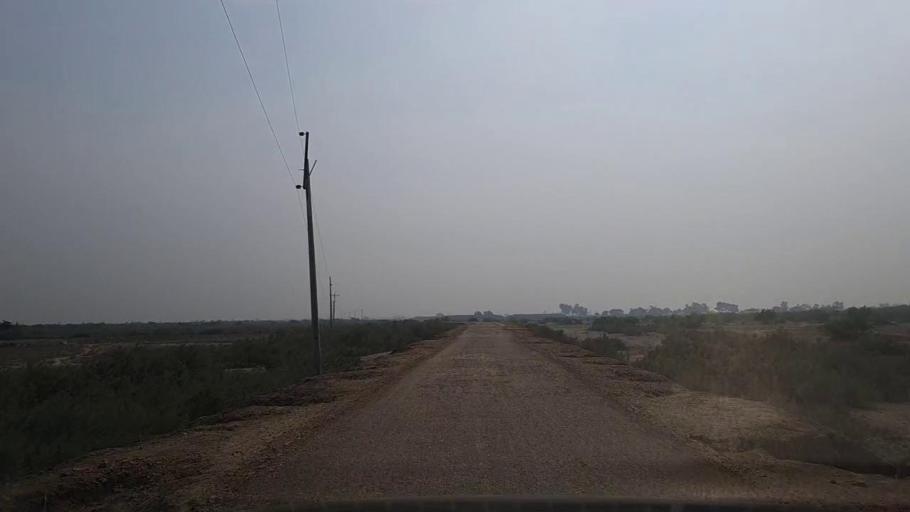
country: PK
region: Sindh
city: Mirpur Sakro
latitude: 24.3942
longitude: 67.7513
